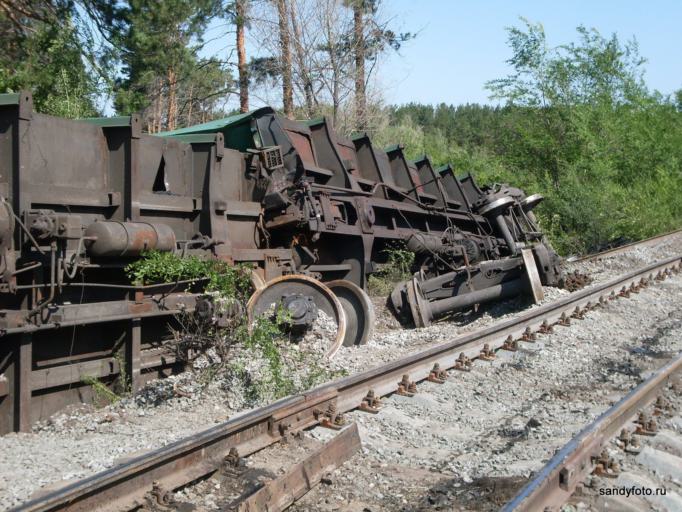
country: RU
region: Chelyabinsk
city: Troitsk
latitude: 54.0510
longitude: 61.6177
